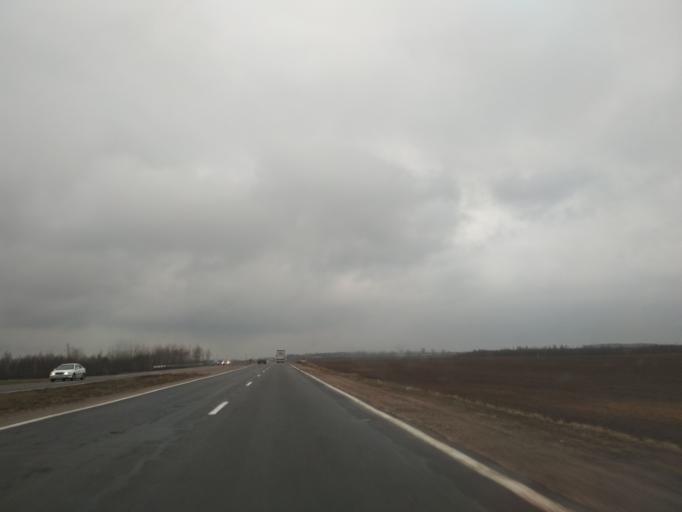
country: BY
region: Minsk
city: Dukora
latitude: 53.6467
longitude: 27.9825
